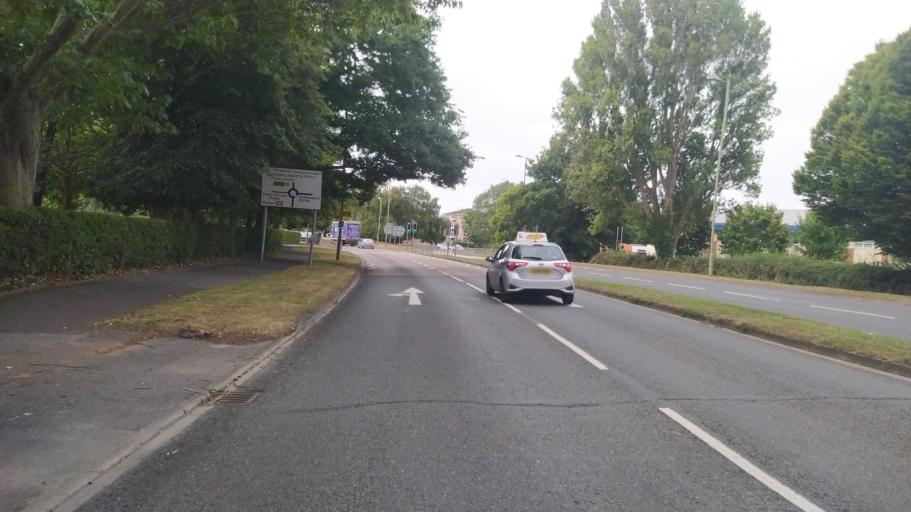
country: GB
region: England
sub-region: Hampshire
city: Havant
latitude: 50.8577
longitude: -0.9850
